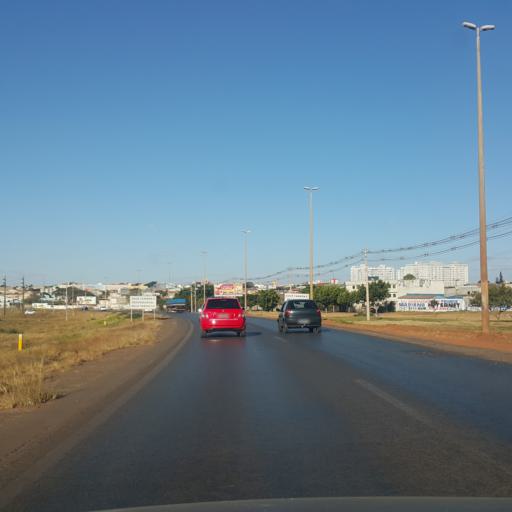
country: BR
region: Federal District
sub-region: Brasilia
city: Brasilia
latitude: -15.8023
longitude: -48.0828
